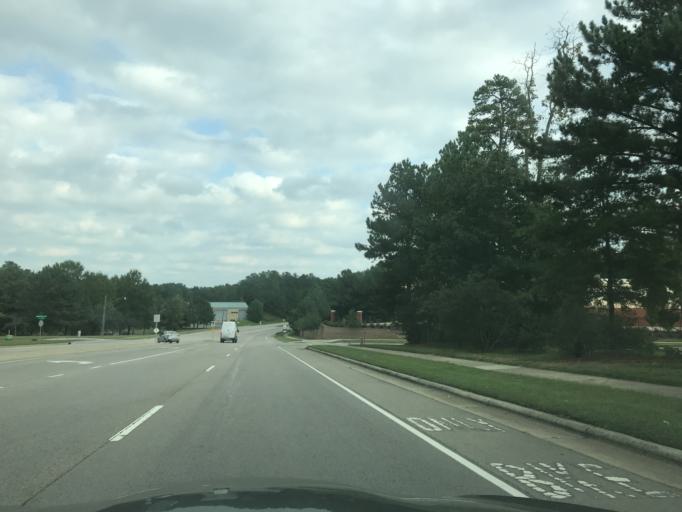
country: US
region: North Carolina
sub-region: Durham County
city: Durham
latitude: 35.9389
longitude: -78.9041
